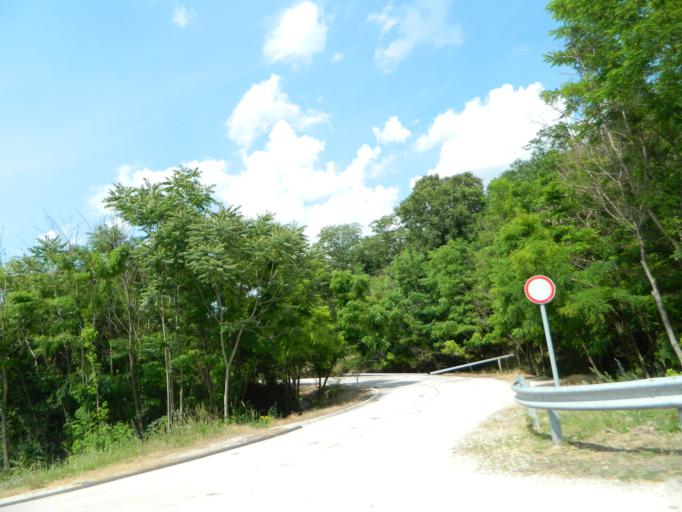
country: HU
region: Somogy
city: Balatonfoldvar
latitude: 46.8141
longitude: 17.9100
